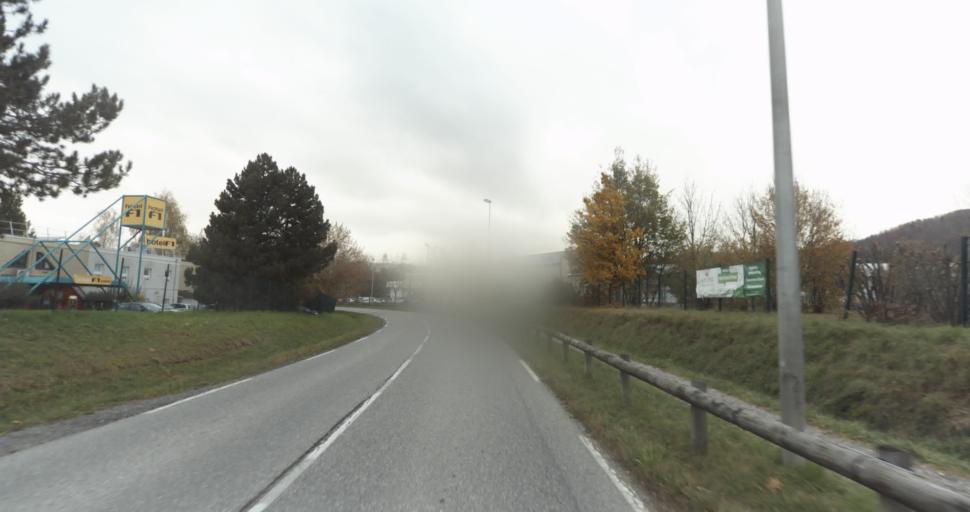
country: FR
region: Rhone-Alpes
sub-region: Departement de la Haute-Savoie
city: Pringy
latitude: 45.9431
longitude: 6.1332
